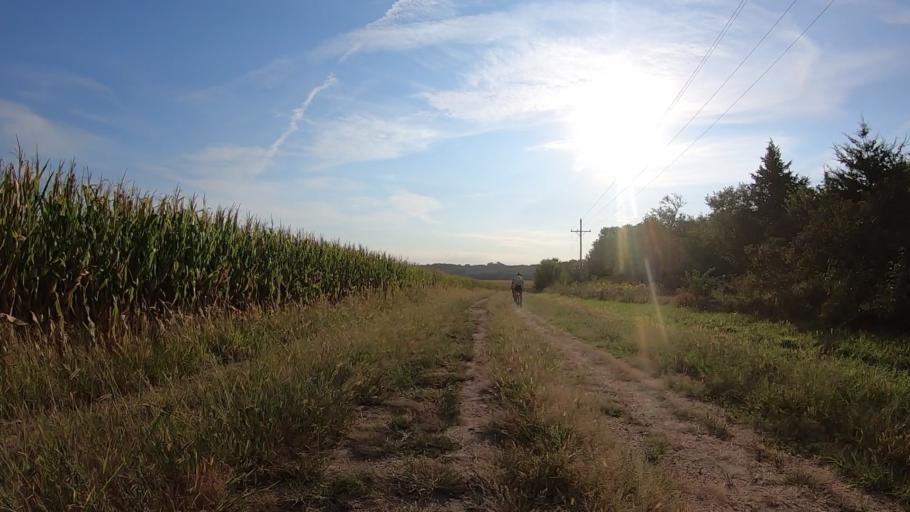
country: US
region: Kansas
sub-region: Marshall County
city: Blue Rapids
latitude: 39.7119
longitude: -96.7826
